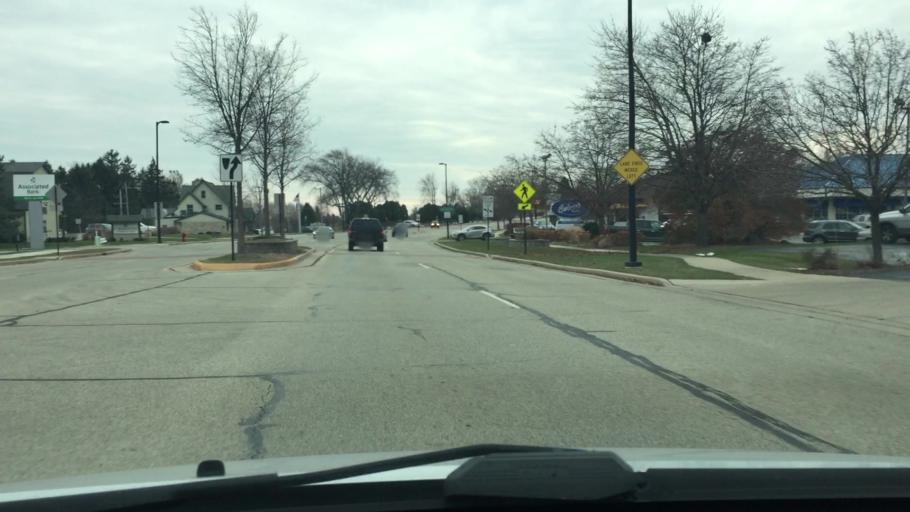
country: US
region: Wisconsin
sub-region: Ozaukee County
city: Grafton
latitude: 43.3054
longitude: -87.9601
